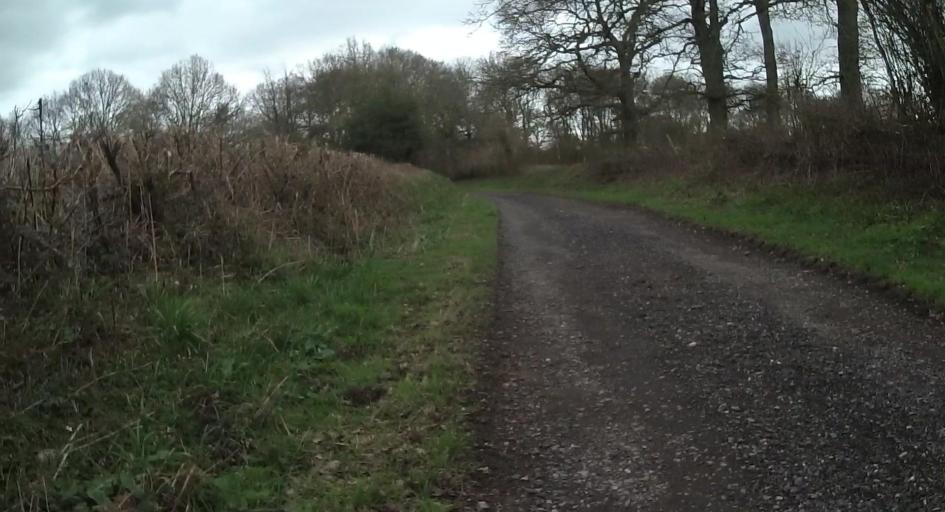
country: GB
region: England
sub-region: Hampshire
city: Basingstoke
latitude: 51.1960
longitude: -1.0576
